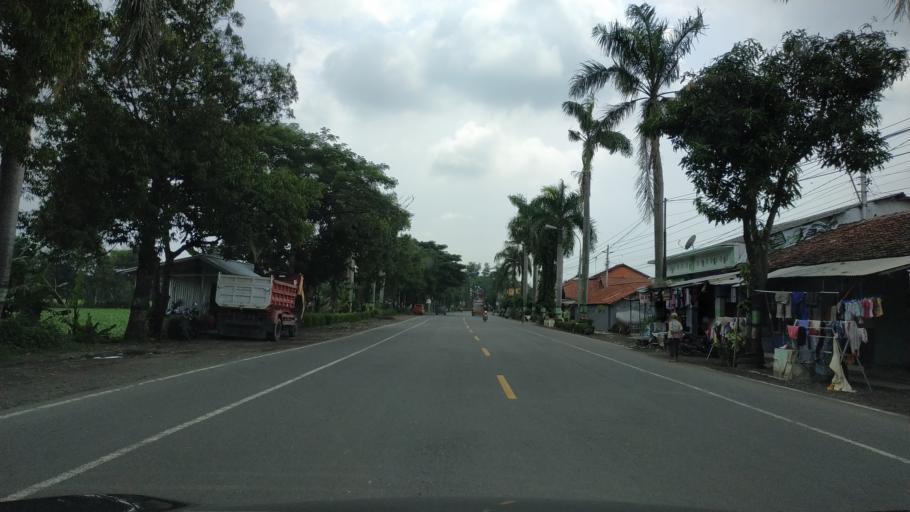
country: ID
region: Central Java
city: Slawi
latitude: -7.0005
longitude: 109.1408
